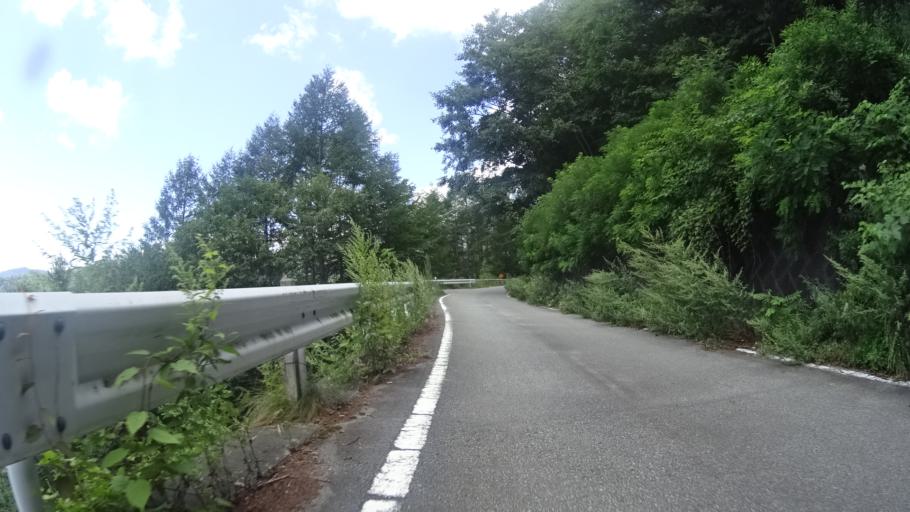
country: JP
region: Yamanashi
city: Enzan
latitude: 35.8307
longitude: 138.6391
